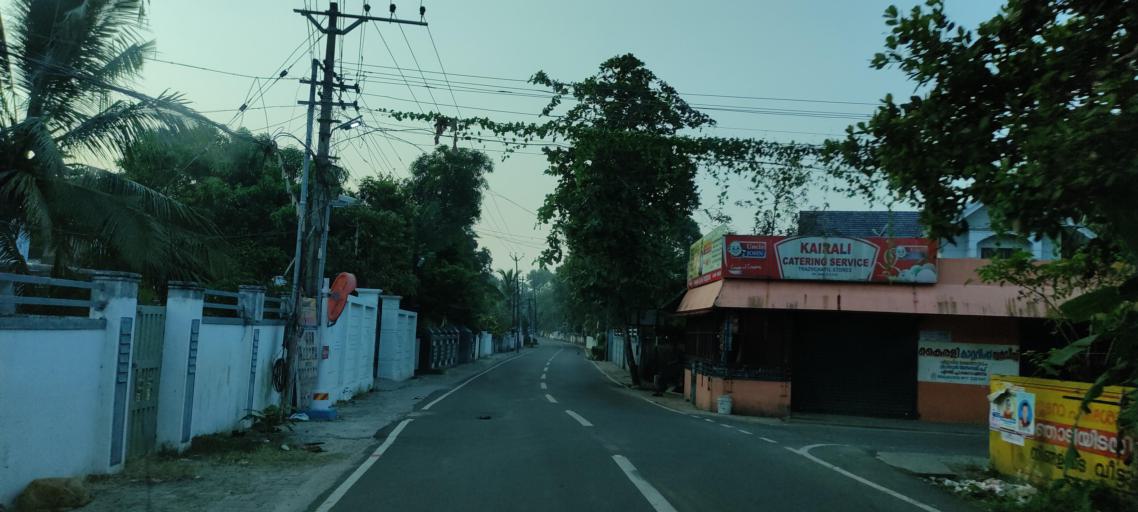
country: IN
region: Kerala
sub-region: Alappuzha
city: Alleppey
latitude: 9.4509
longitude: 76.3451
